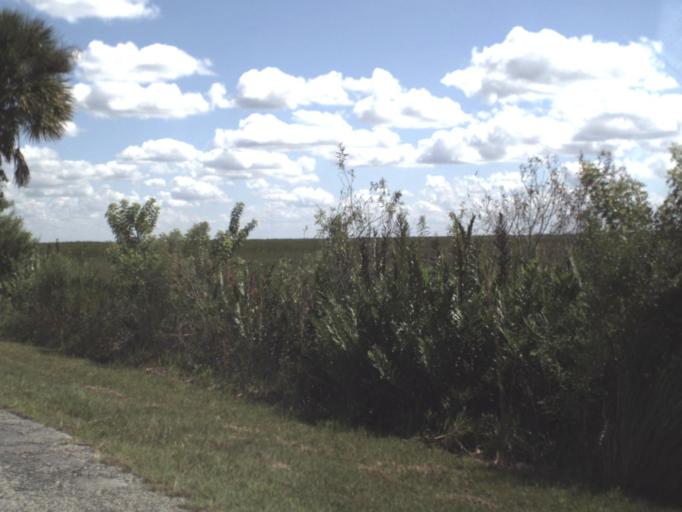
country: US
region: Florida
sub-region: Collier County
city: Marco
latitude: 25.9243
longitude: -81.4203
